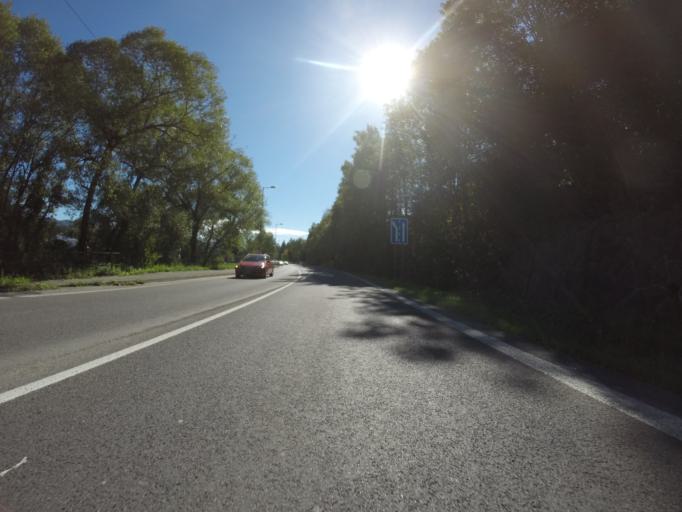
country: SK
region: Trenciansky
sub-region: Okres Povazska Bystrica
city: Povazska Bystrica
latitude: 49.1012
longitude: 18.4597
